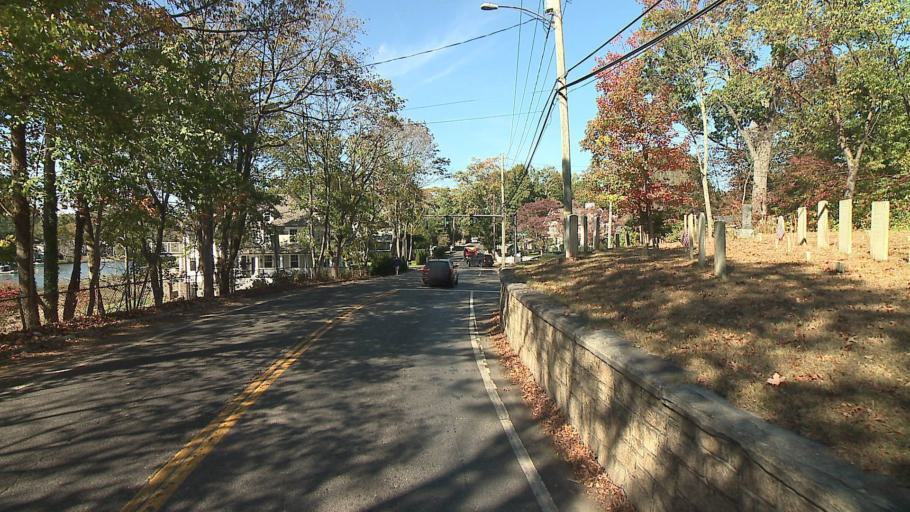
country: US
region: Connecticut
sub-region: Fairfield County
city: Darien
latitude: 41.0714
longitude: -73.4451
